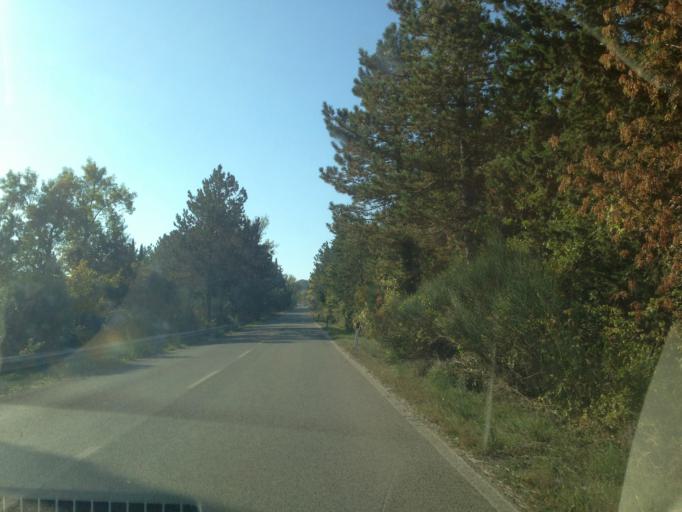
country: IT
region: Tuscany
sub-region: Provincia di Siena
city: Castellina in Chianti
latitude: 43.4878
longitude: 11.2994
